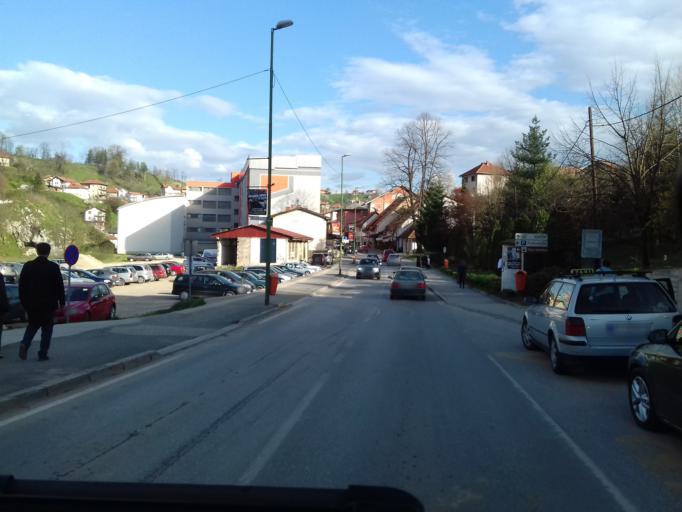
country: BA
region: Federation of Bosnia and Herzegovina
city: Tesanj
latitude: 44.6098
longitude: 17.9884
